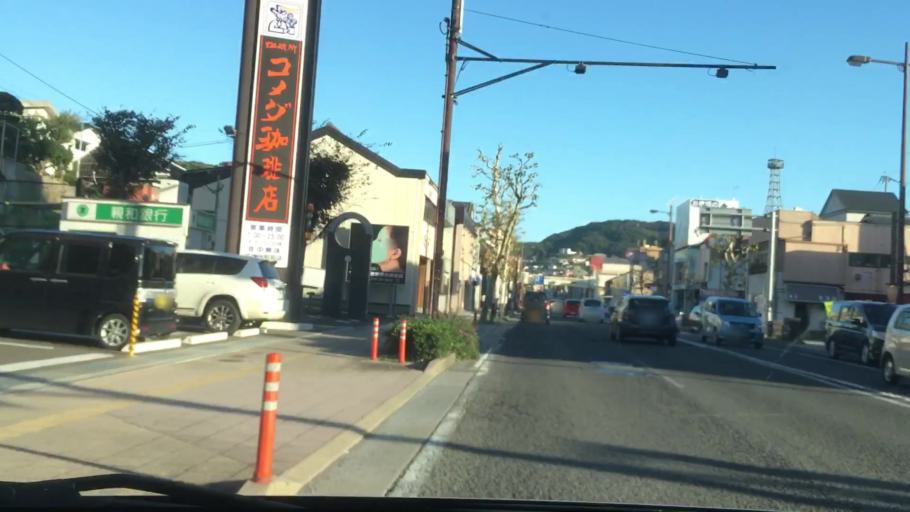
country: JP
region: Nagasaki
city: Sasebo
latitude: 33.1622
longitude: 129.7295
